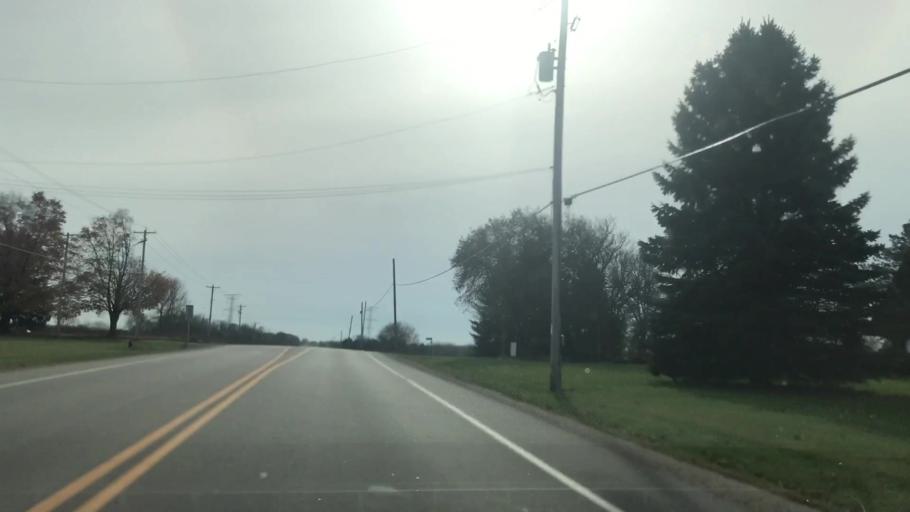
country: US
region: Wisconsin
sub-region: Waukesha County
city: Menomonee Falls
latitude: 43.2041
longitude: -88.1543
